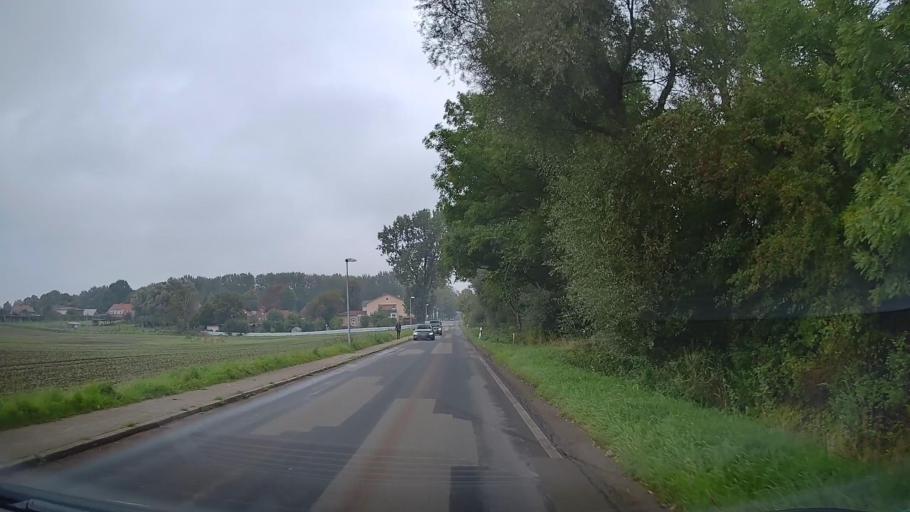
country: DE
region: Mecklenburg-Vorpommern
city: Hornstorf
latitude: 53.9152
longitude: 11.5327
